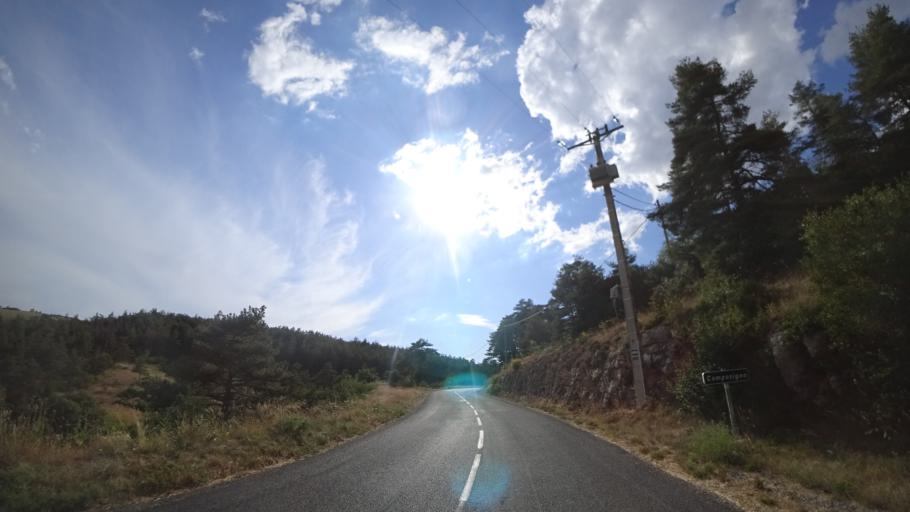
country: FR
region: Languedoc-Roussillon
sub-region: Departement de la Lozere
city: Chanac
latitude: 44.3733
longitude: 3.3384
